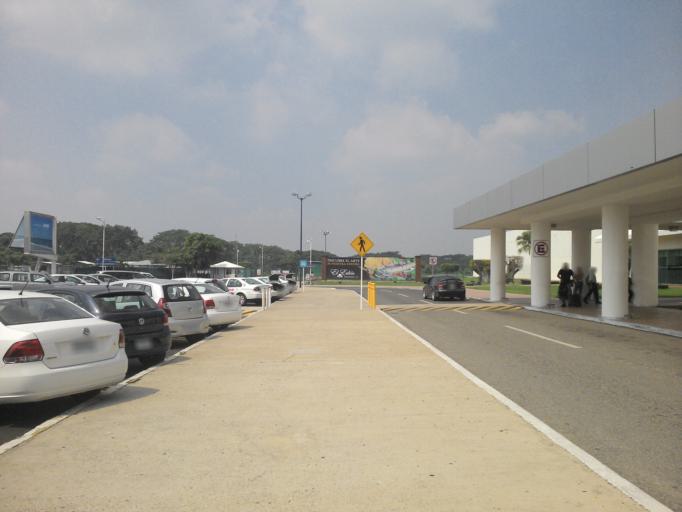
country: MX
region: Tabasco
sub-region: Centro
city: El Bajio
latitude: 17.9925
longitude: -92.8190
